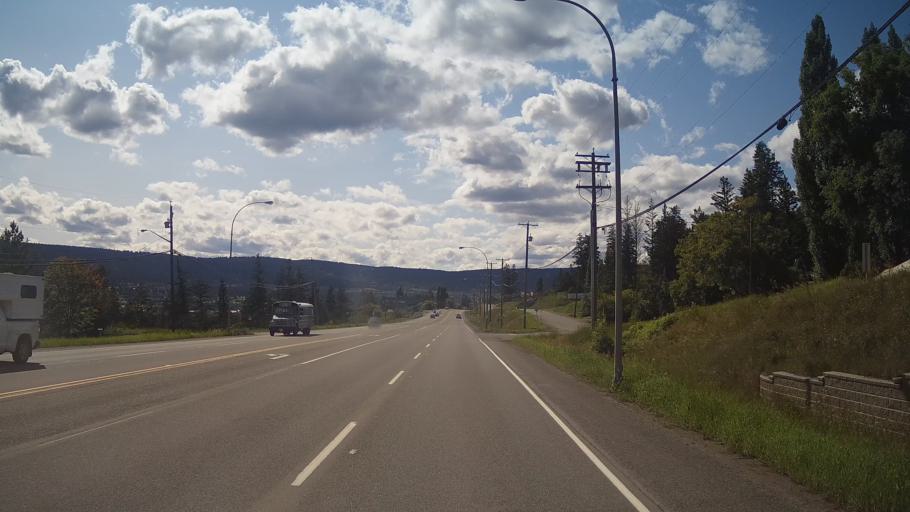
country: CA
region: British Columbia
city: Williams Lake
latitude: 52.1222
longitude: -122.1020
